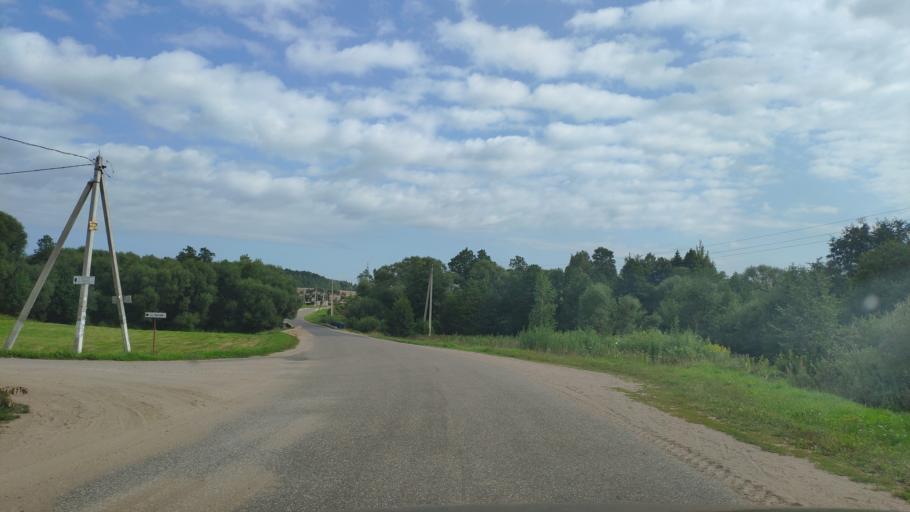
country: BY
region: Minsk
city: Khatsyezhyna
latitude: 53.8650
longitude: 27.3168
